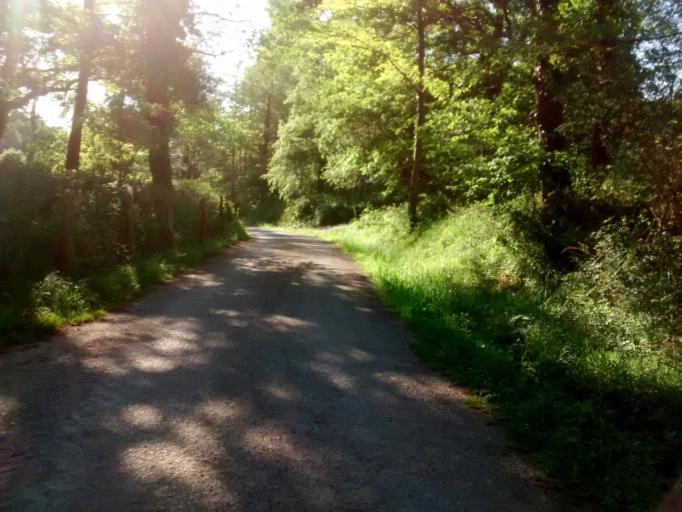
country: ES
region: Cantabria
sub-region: Provincia de Cantabria
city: Entrambasaguas
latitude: 43.3386
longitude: -3.6650
